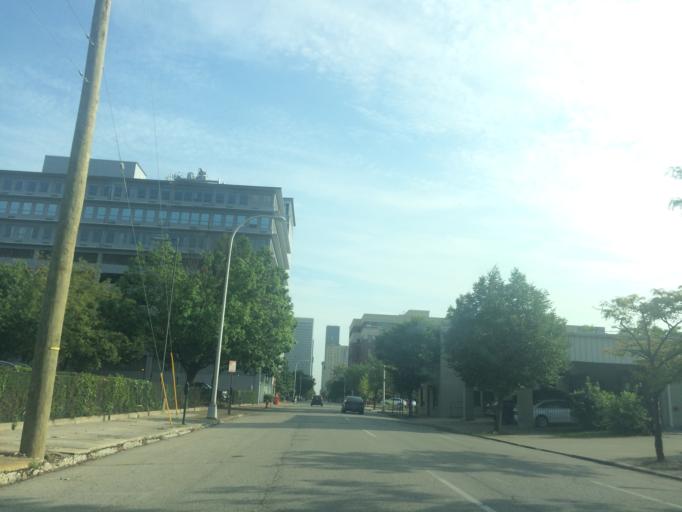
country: US
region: Kentucky
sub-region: Jefferson County
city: Louisville
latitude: 38.2448
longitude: -85.7603
